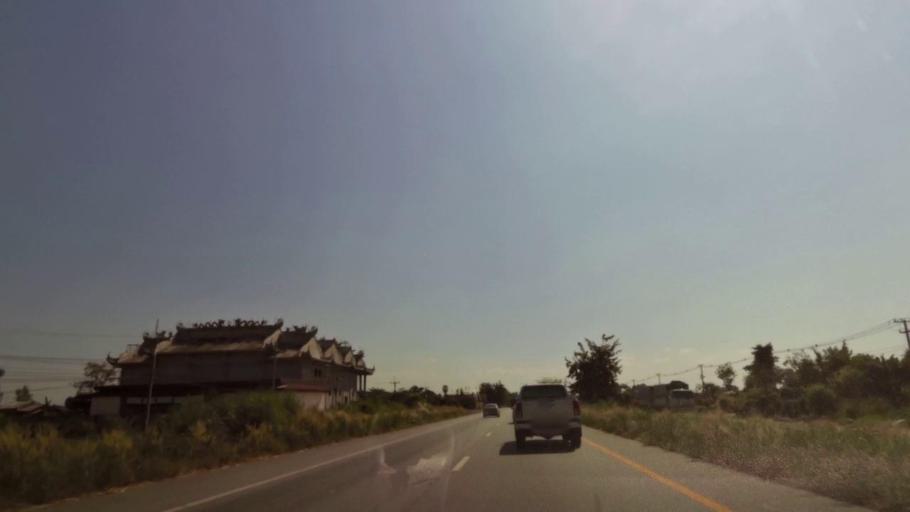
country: TH
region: Nakhon Sawan
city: Kao Liao
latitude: 15.8282
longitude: 100.1188
